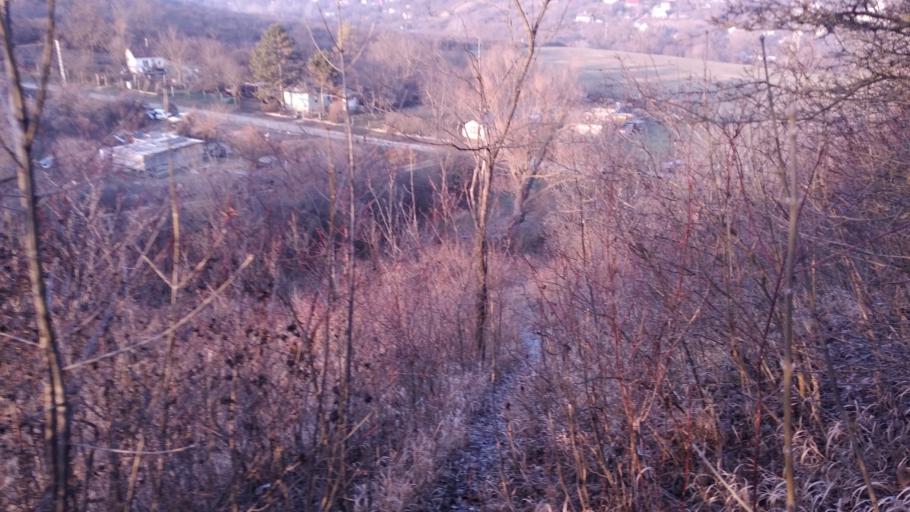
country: HU
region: Pest
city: Budakalasz
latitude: 47.6209
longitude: 19.0305
